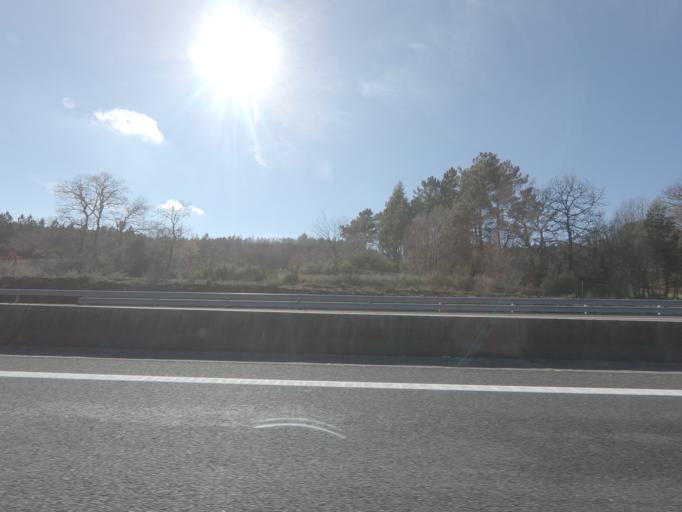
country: ES
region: Galicia
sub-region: Provincia de Ourense
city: Pinor
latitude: 42.5395
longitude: -8.0177
